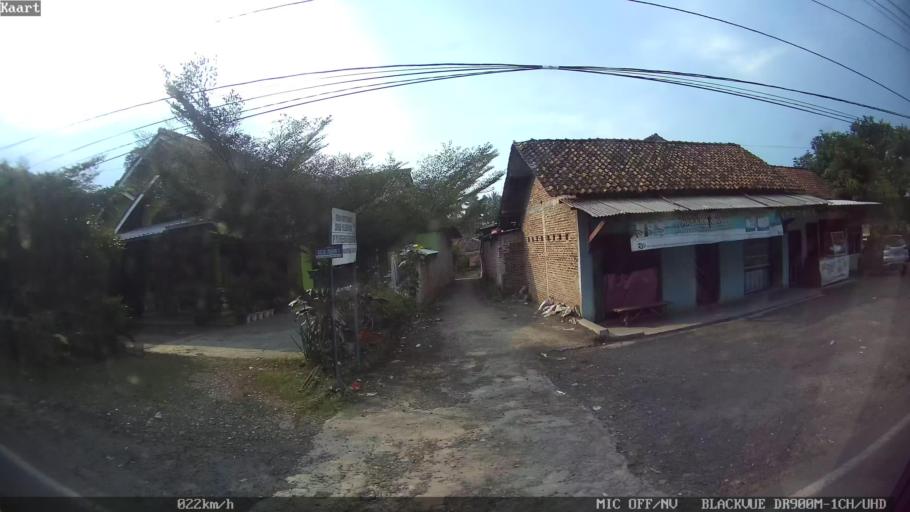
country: ID
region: Lampung
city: Natar
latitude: -5.3693
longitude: 105.1757
